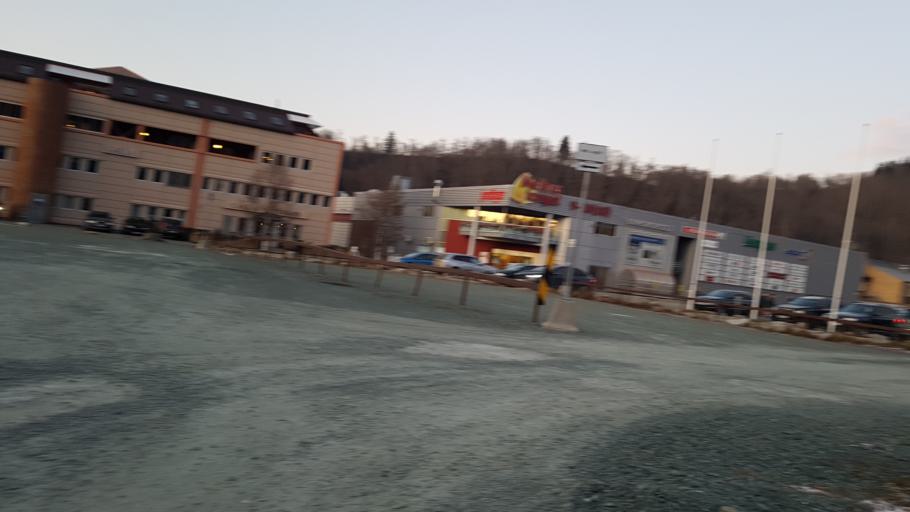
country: NO
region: Sor-Trondelag
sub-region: Melhus
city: Melhus
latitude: 63.2855
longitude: 10.2792
